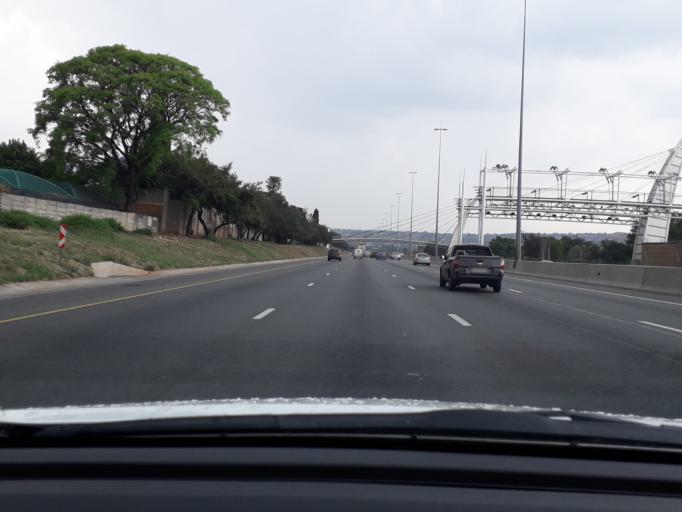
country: ZA
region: Gauteng
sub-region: City of Johannesburg Metropolitan Municipality
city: Roodepoort
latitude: -26.1308
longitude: 27.9391
